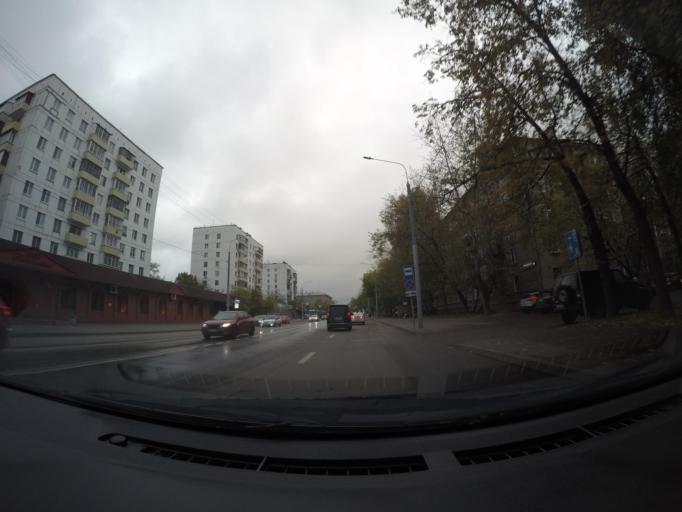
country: RU
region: Moskovskaya
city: Novogireyevo
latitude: 55.7579
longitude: 37.7959
